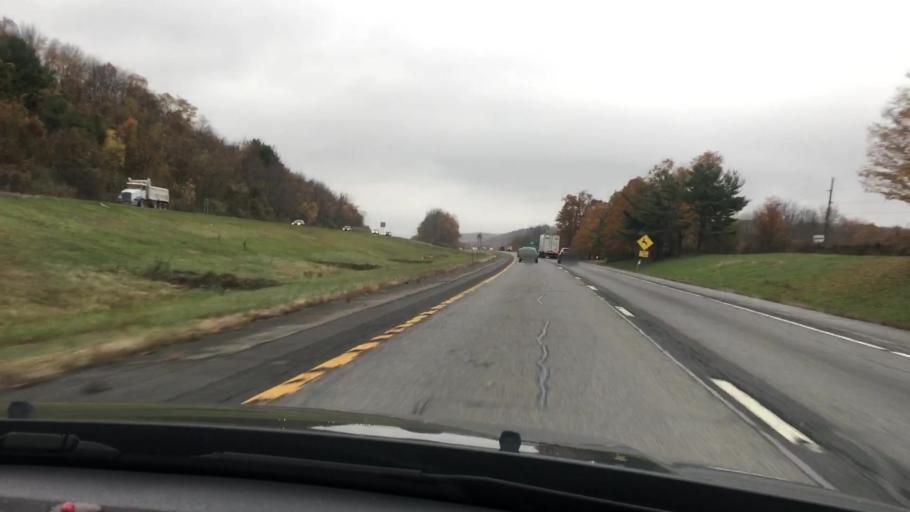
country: US
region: New York
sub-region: Putnam County
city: Lake Carmel
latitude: 41.4673
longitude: -73.6449
